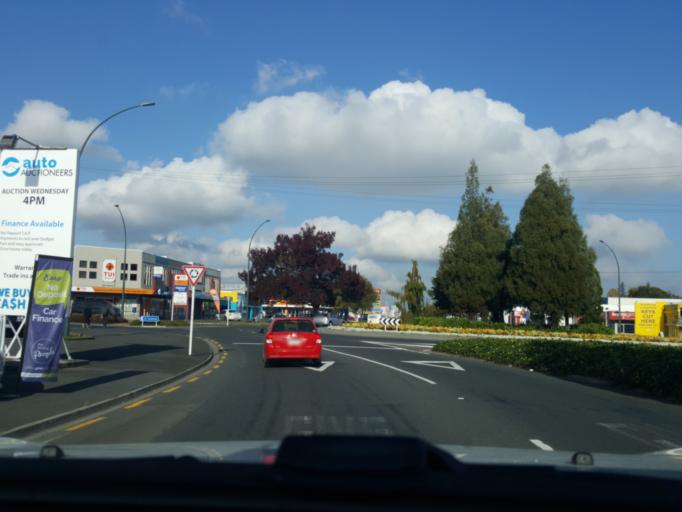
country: NZ
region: Waikato
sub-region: Hamilton City
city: Hamilton
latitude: -37.7573
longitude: 175.2458
